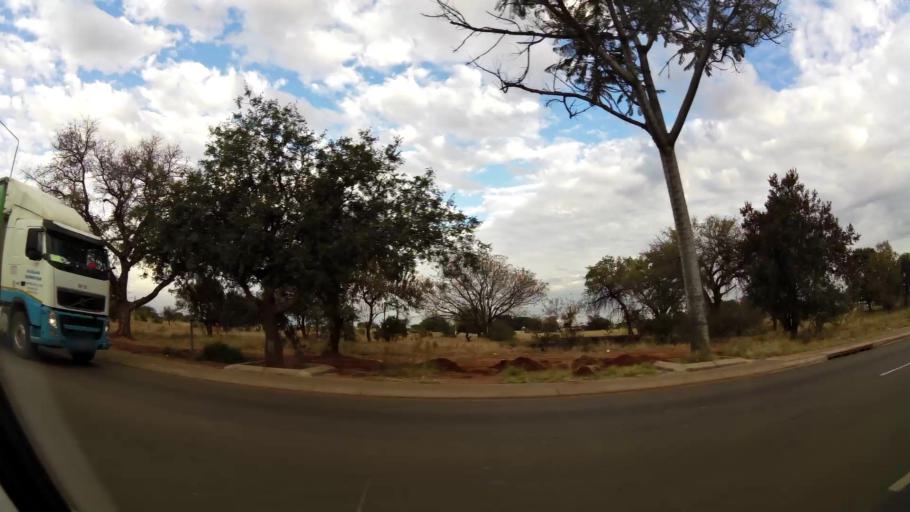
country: ZA
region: Limpopo
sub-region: Waterberg District Municipality
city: Modimolle
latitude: -24.5123
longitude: 28.7216
